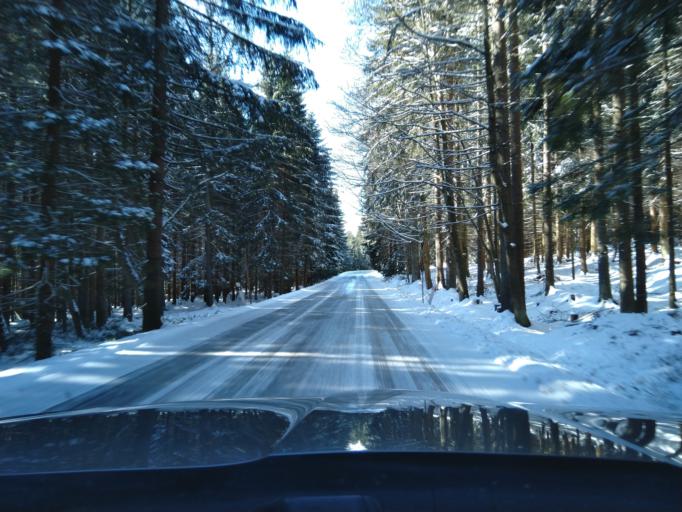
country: CZ
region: Jihocesky
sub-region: Okres Prachatice
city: Stachy
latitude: 49.0570
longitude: 13.6438
